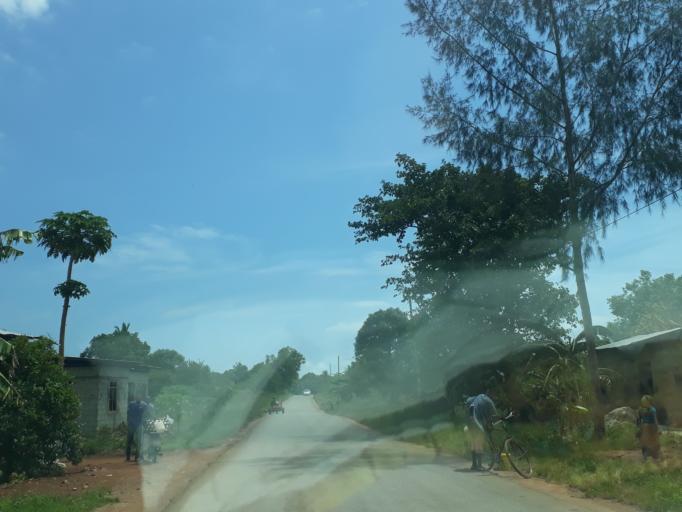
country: TZ
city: Kiwengwa
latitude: -5.9941
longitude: 39.3472
